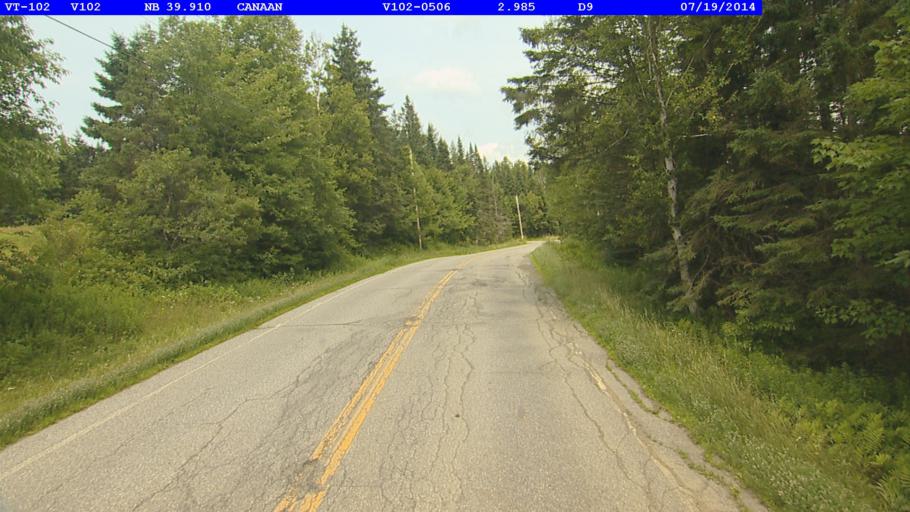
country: US
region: New Hampshire
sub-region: Coos County
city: Colebrook
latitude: 44.9493
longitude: -71.5255
